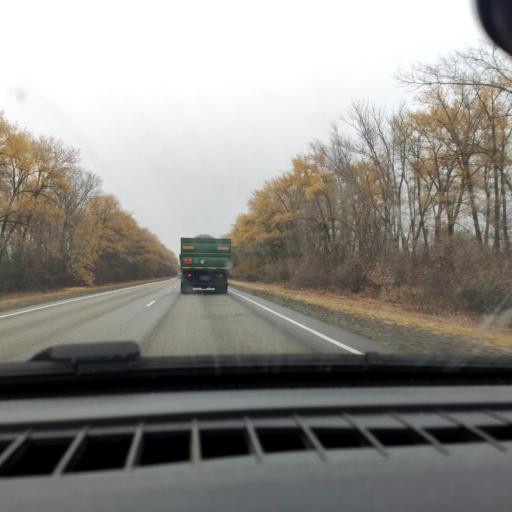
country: RU
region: Voronezj
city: Ostrogozhsk
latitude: 50.9871
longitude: 38.9967
